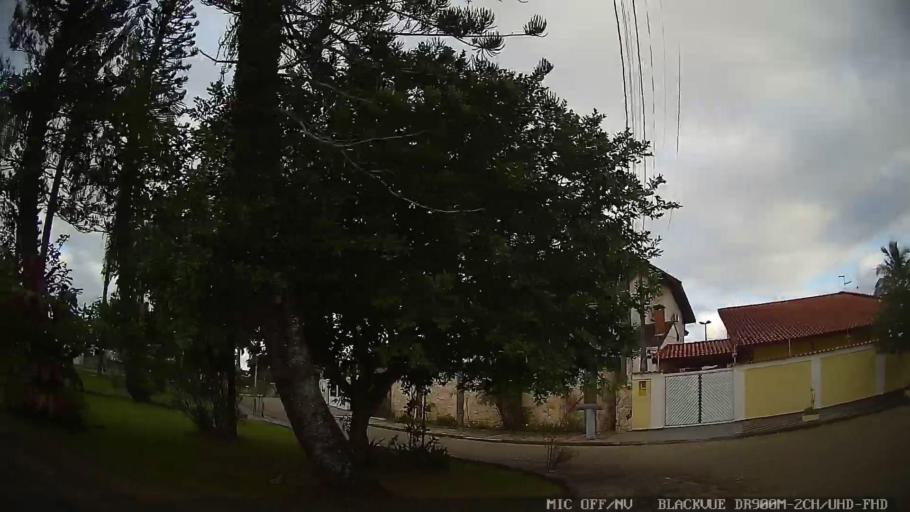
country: BR
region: Sao Paulo
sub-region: Peruibe
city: Peruibe
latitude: -24.3082
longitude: -46.9900
